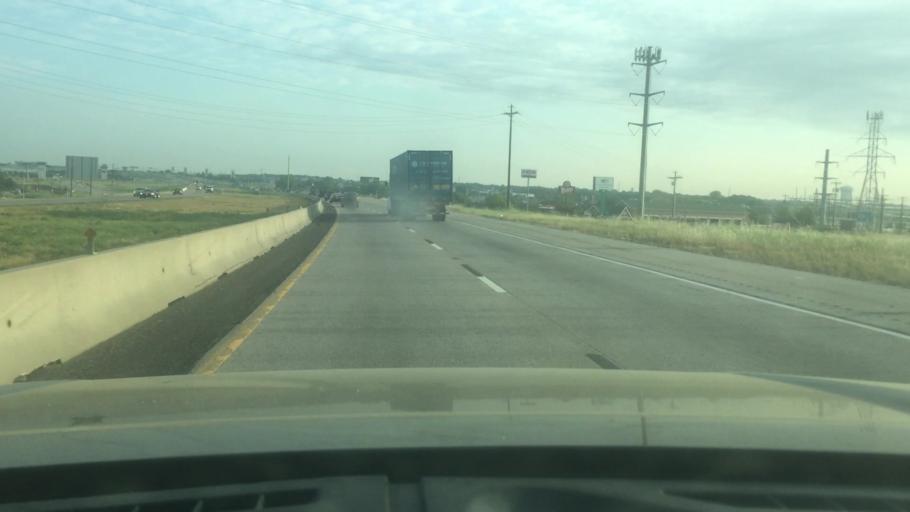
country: US
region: Texas
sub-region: Tarrant County
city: Euless
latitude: 32.8634
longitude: -97.1026
